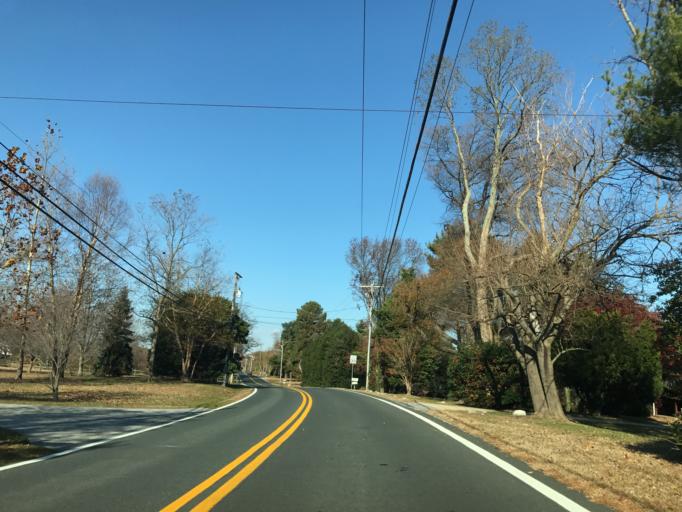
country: US
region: Maryland
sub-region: Anne Arundel County
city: Cape Saint Claire
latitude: 39.0916
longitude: -76.4260
